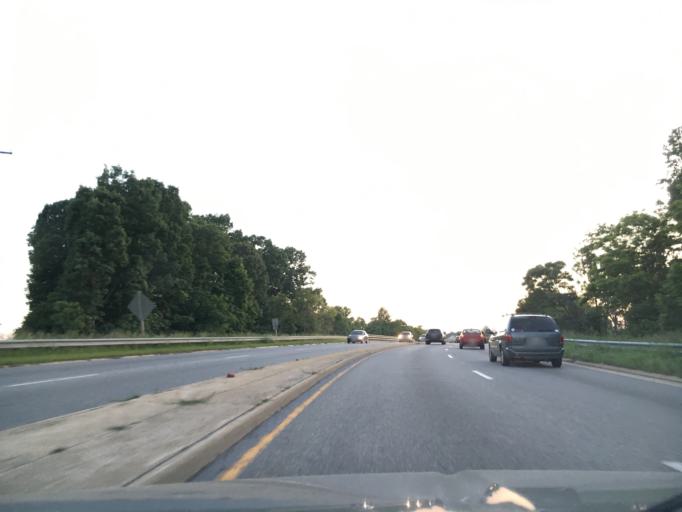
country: US
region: Virginia
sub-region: Bedford County
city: Forest
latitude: 37.3690
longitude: -79.2546
